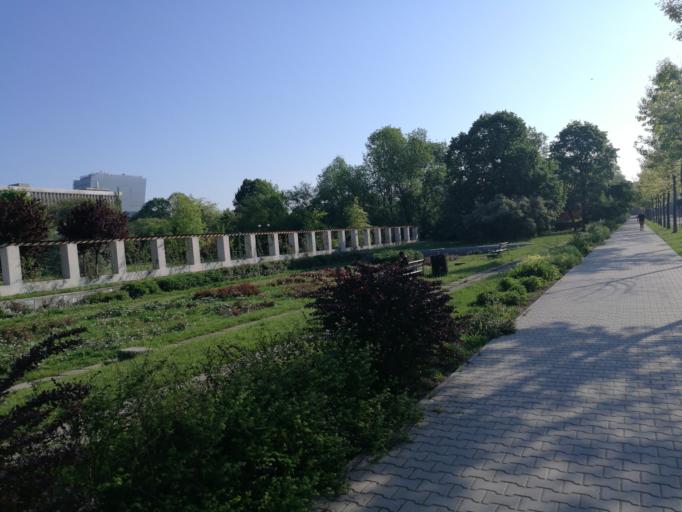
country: RO
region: Bucuresti
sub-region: Municipiul Bucuresti
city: Bucuresti
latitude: 44.4702
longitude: 26.0658
